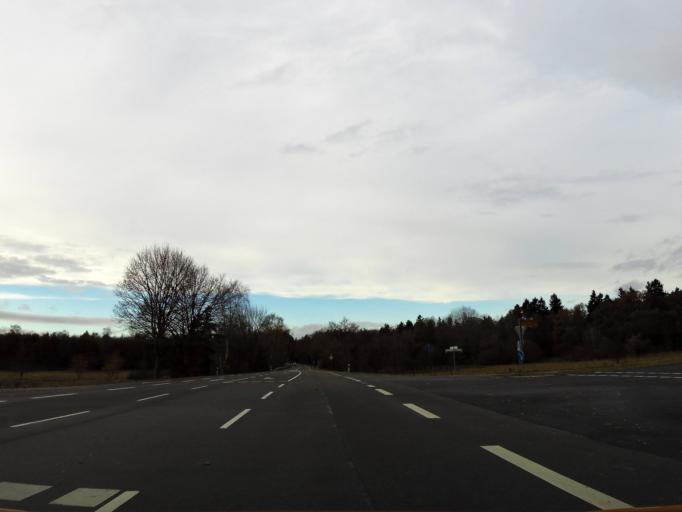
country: DE
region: Lower Saxony
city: Eimke
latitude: 52.9828
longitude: 10.2521
